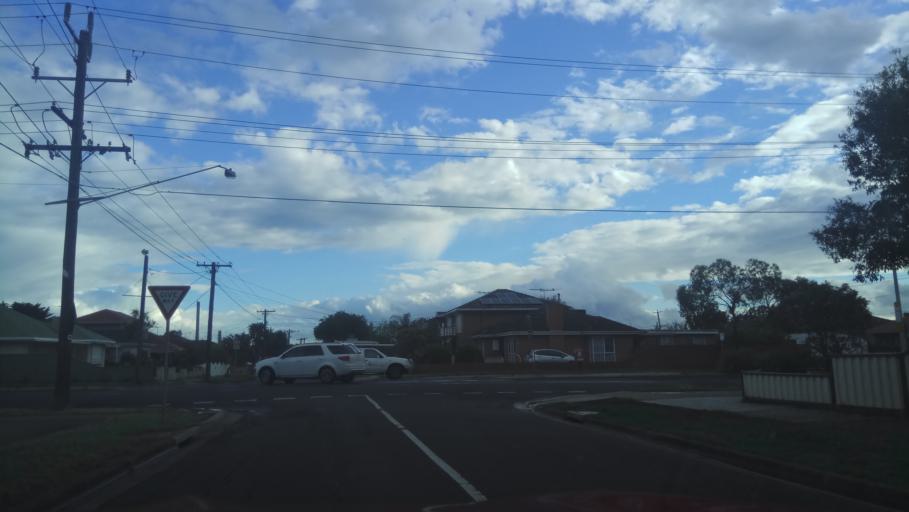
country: AU
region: Victoria
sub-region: Hobsons Bay
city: Altona North
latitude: -37.8382
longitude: 144.8481
